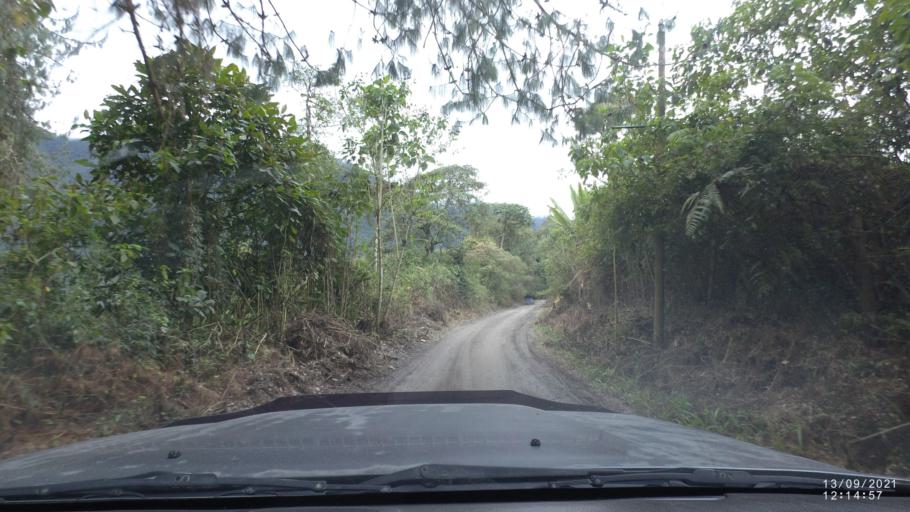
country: BO
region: Cochabamba
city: Colomi
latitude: -17.2228
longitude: -65.8245
